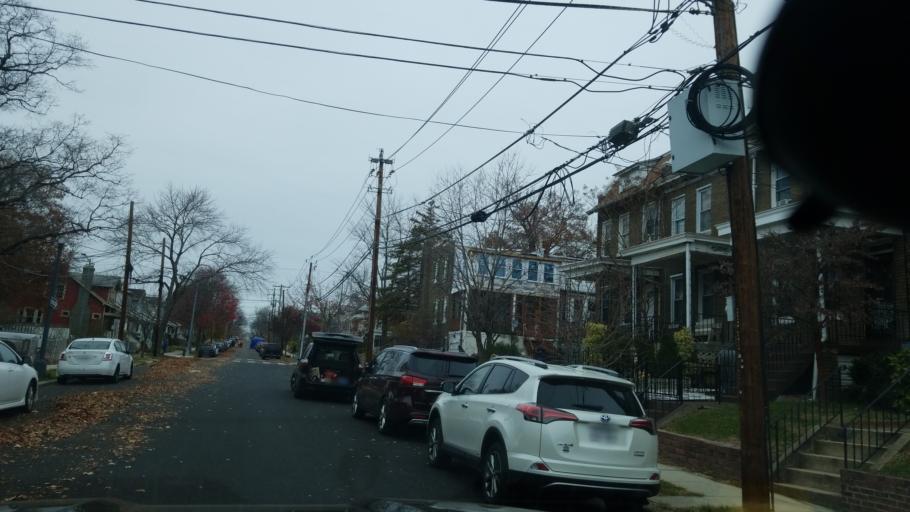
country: US
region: Maryland
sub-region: Prince George's County
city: Chillum
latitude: 38.9404
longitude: -77.0170
